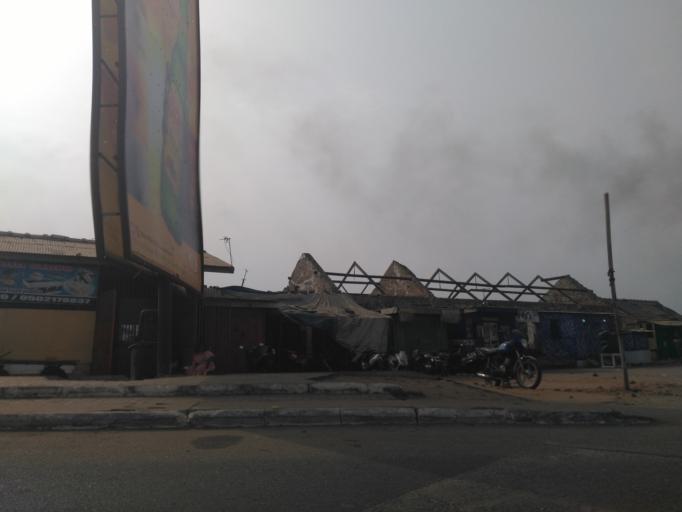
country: GH
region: Greater Accra
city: Accra
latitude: 5.5331
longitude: -0.2126
